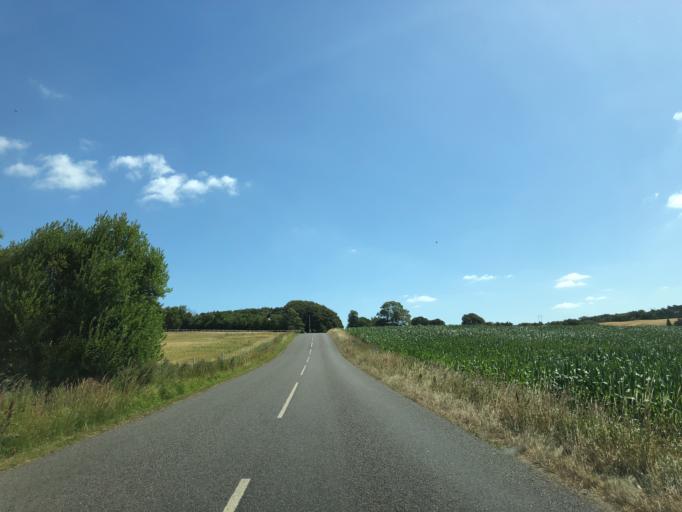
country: DK
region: North Denmark
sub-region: Vesthimmerland Kommune
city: Alestrup
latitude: 56.5758
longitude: 9.5201
